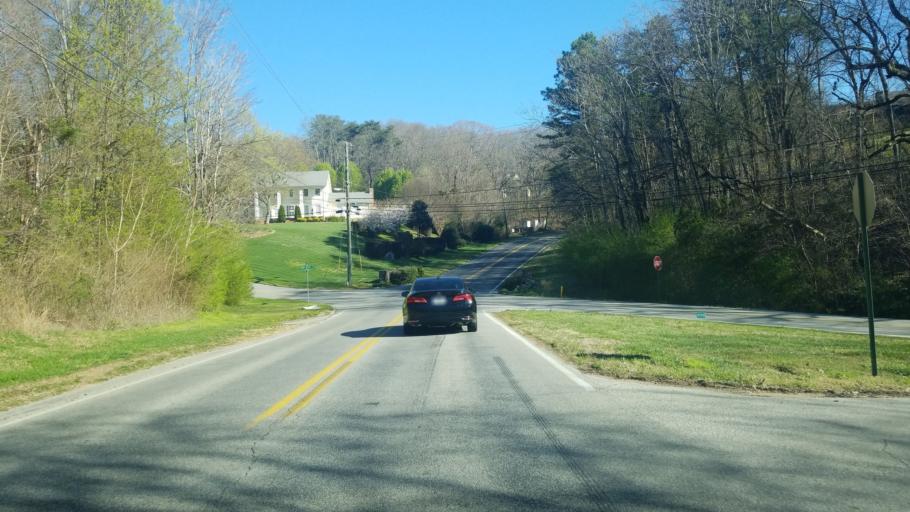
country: US
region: Tennessee
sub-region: Hamilton County
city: East Chattanooga
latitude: 35.1186
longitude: -85.2115
